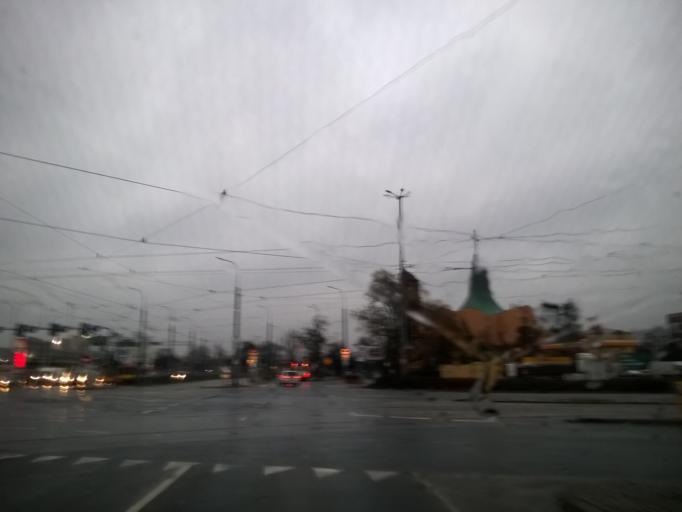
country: PL
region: Lower Silesian Voivodeship
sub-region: Powiat wroclawski
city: Wroclaw
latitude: 51.0832
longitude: 17.0494
